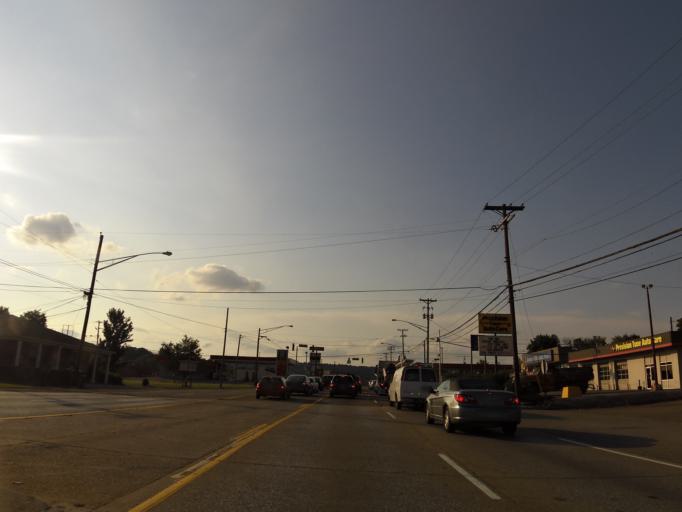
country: US
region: Tennessee
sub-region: Knox County
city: Knoxville
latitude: 36.0241
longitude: -83.9263
